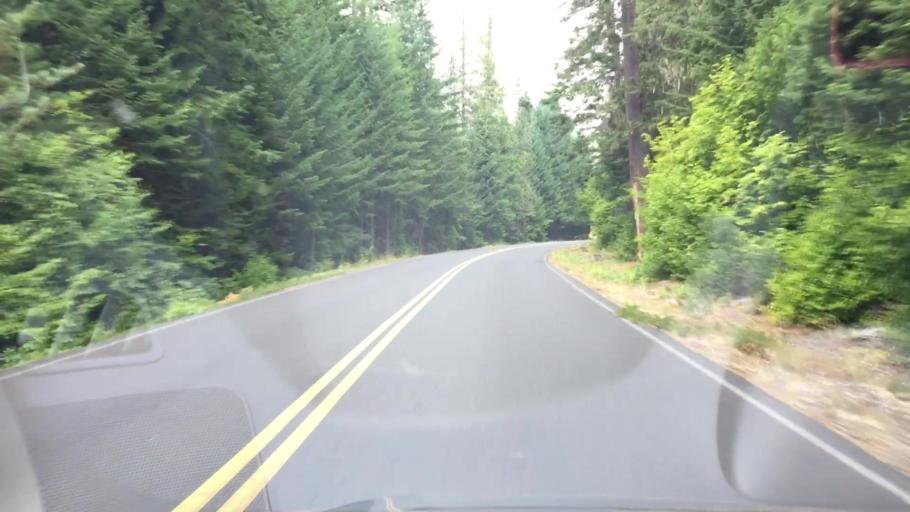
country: US
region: Washington
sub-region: Klickitat County
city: White Salmon
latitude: 46.0632
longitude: -121.5709
